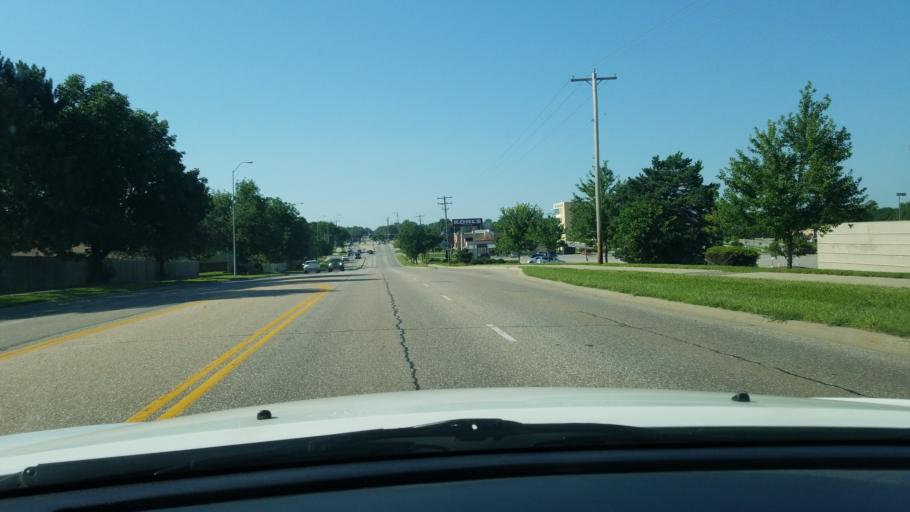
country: US
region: Nebraska
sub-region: Lancaster County
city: Lincoln
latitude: 40.8173
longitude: -96.6060
